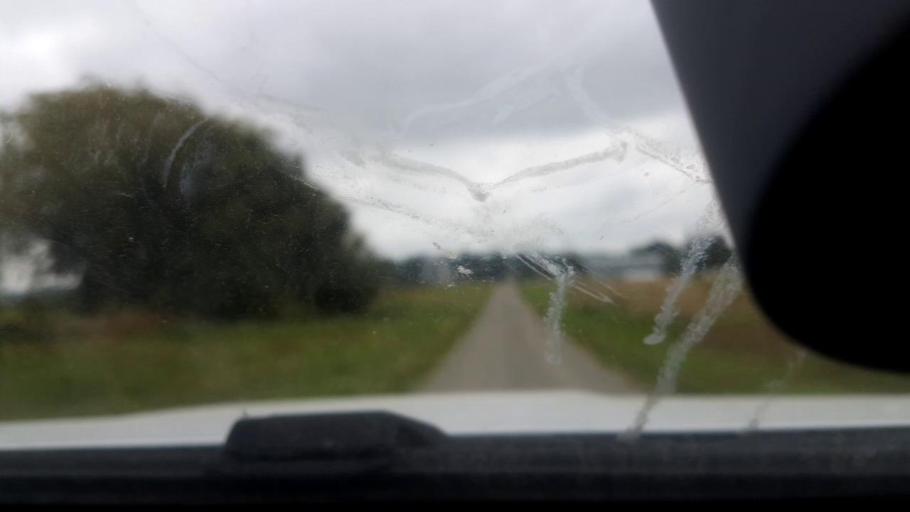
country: NZ
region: Canterbury
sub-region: Timaru District
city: Pleasant Point
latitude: -44.2260
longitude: 171.1646
